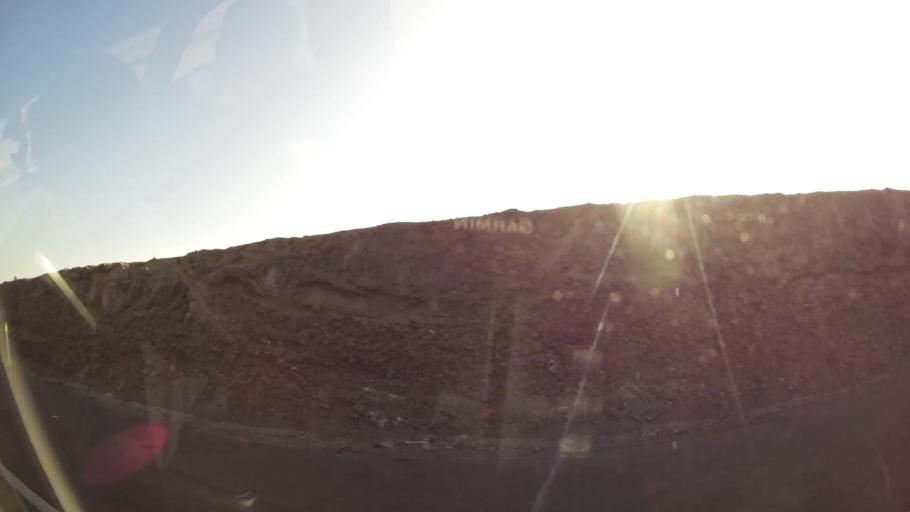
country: PE
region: Ica
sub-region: Provincia de Pisco
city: San Clemente
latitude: -13.6444
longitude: -76.1735
